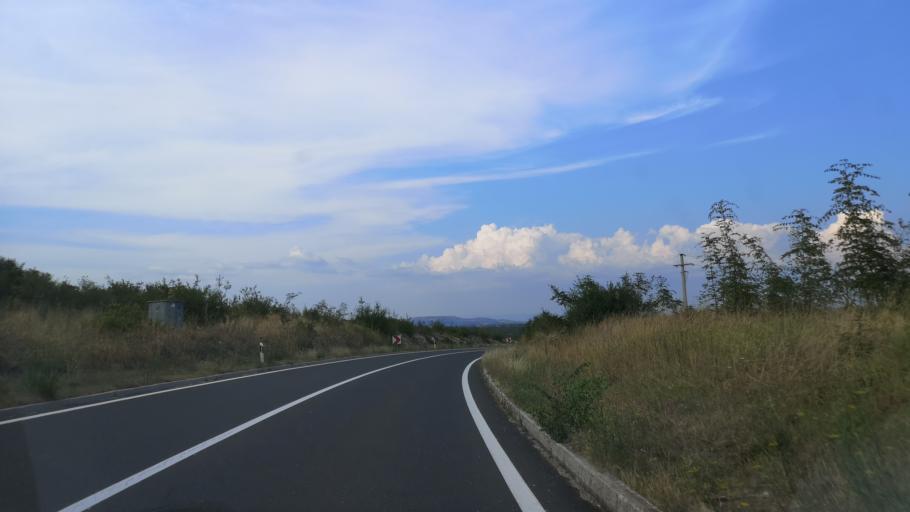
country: HR
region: Sibensko-Kniniska
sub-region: Grad Sibenik
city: Pirovac
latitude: 43.8766
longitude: 15.7415
